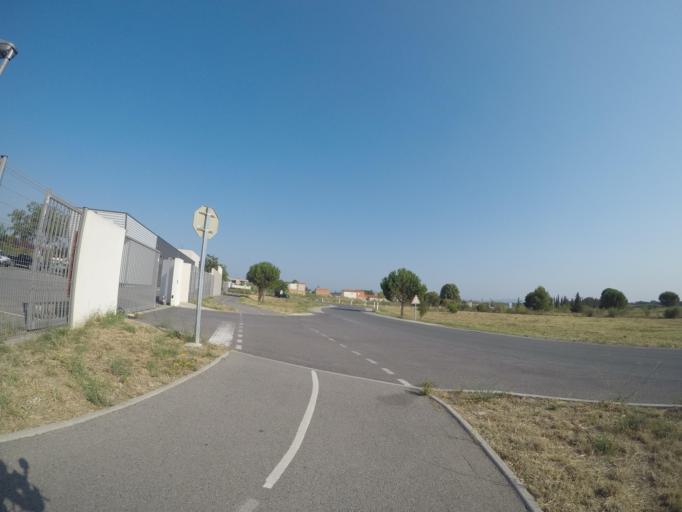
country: FR
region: Languedoc-Roussillon
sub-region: Departement des Pyrenees-Orientales
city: Llupia
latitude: 42.6234
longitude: 2.7717
